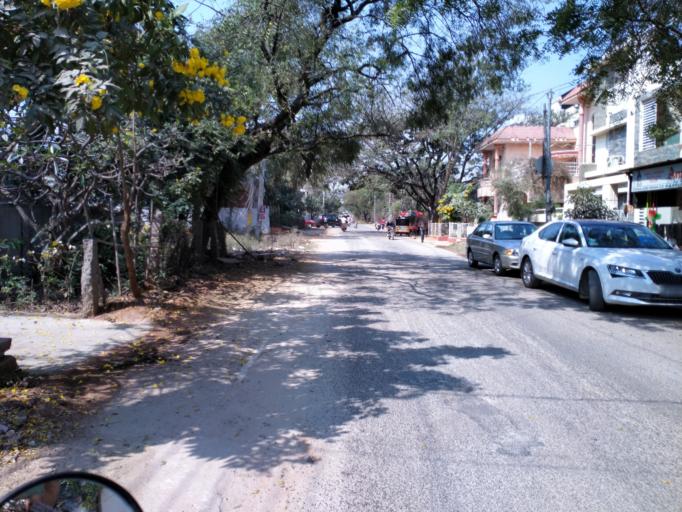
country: IN
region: Telangana
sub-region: Rangareddi
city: Secunderabad
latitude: 17.5023
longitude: 78.5479
